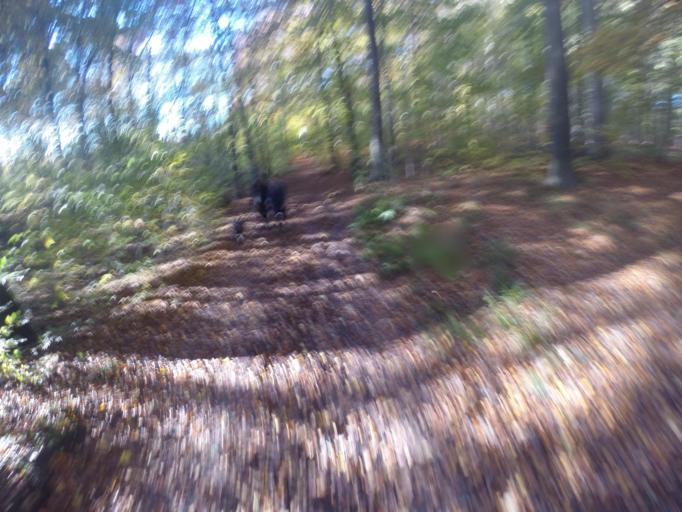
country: DK
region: Capital Region
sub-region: Rudersdal Kommune
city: Holte
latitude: 55.7768
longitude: 12.4436
